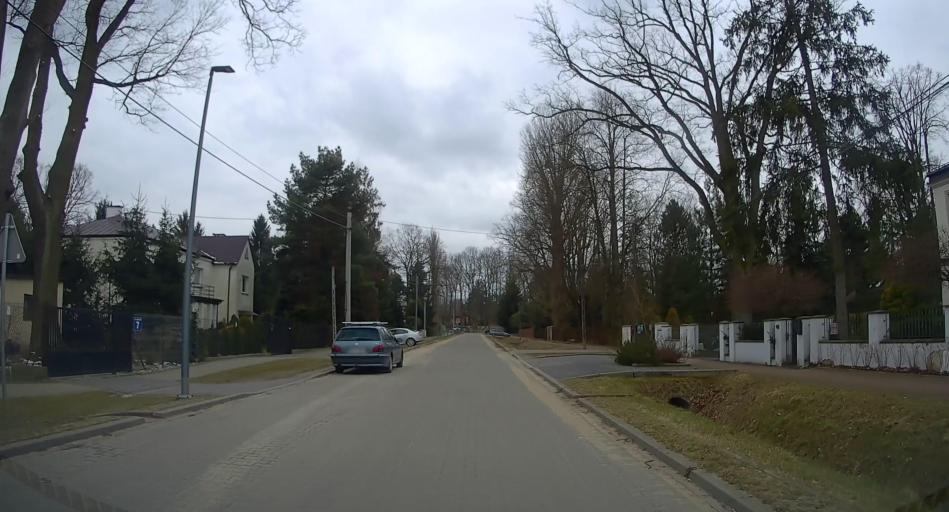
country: PL
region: Masovian Voivodeship
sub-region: Powiat piaseczynski
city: Piaseczno
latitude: 52.0604
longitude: 21.0015
